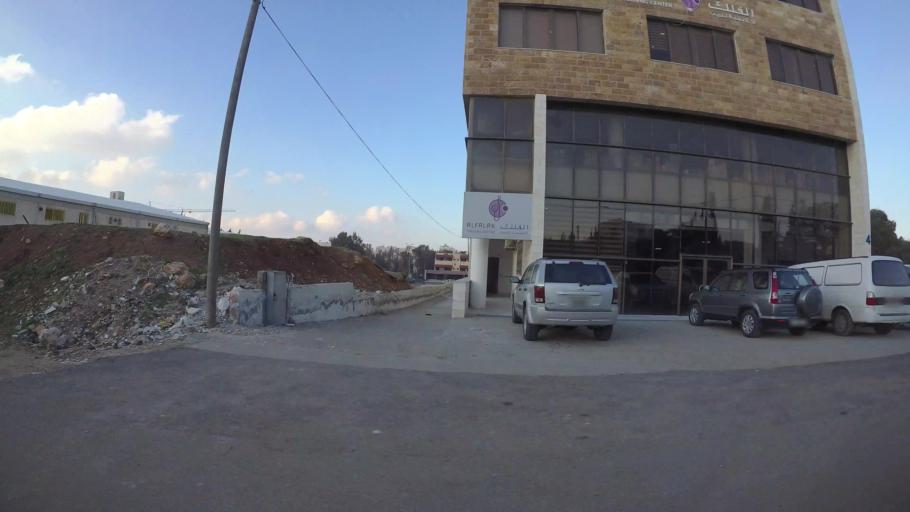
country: JO
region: Amman
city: Al Bunayyat ash Shamaliyah
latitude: 31.9123
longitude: 35.9167
